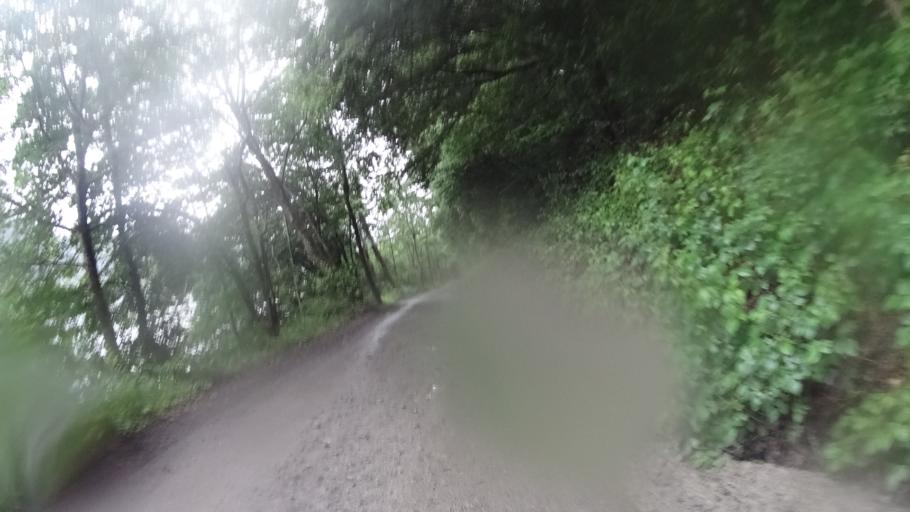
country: DE
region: Bavaria
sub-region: Lower Bavaria
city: Passau
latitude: 48.5213
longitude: 13.4473
